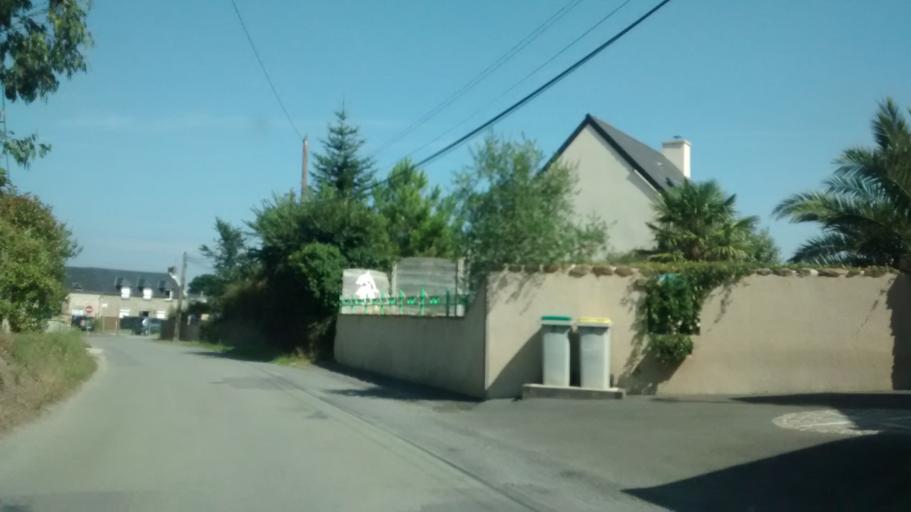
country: FR
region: Brittany
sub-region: Departement d'Ille-et-Vilaine
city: Saint-Coulomb
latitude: 48.6851
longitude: -1.8956
